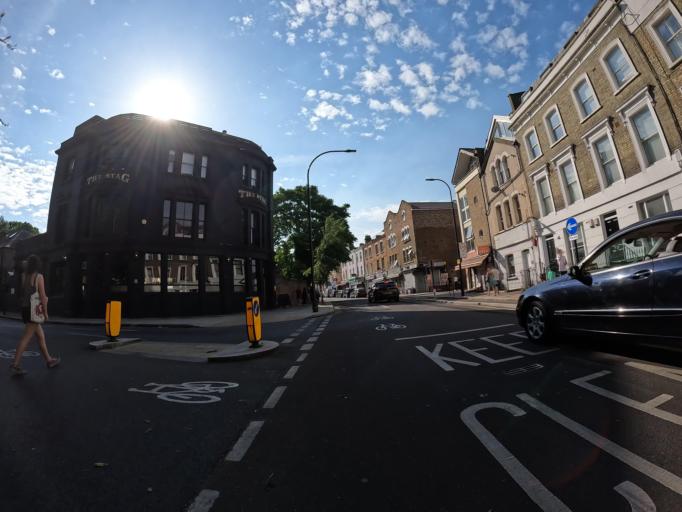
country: GB
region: England
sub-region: Greater London
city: Hendon
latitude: 51.5793
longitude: -0.2022
